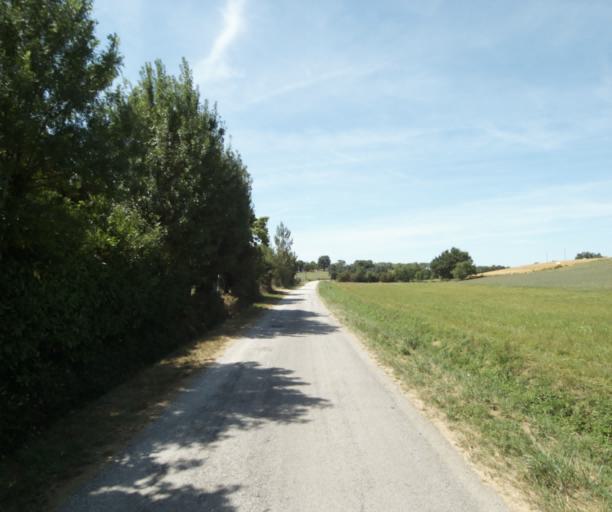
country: FR
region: Midi-Pyrenees
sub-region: Departement de la Haute-Garonne
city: Revel
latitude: 43.4922
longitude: 2.0211
